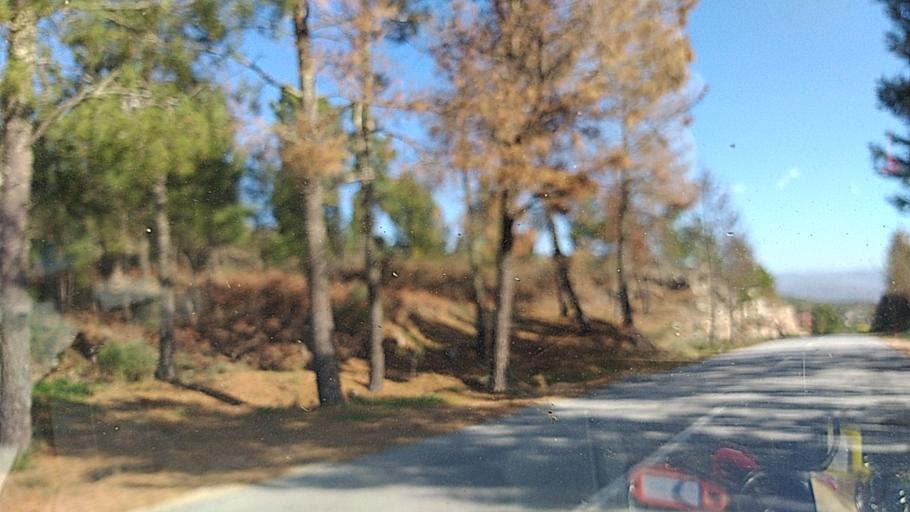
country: PT
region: Guarda
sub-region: Fornos de Algodres
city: Fornos de Algodres
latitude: 40.6370
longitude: -7.4805
